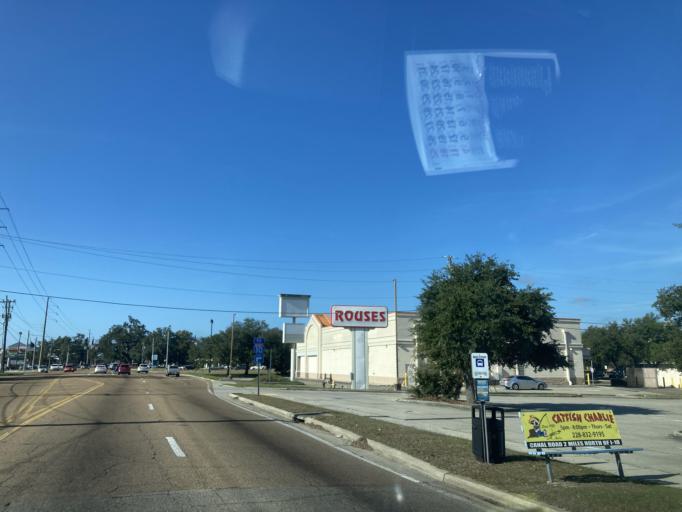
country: US
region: Mississippi
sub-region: Harrison County
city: West Gulfport
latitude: 30.3992
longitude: -89.0250
